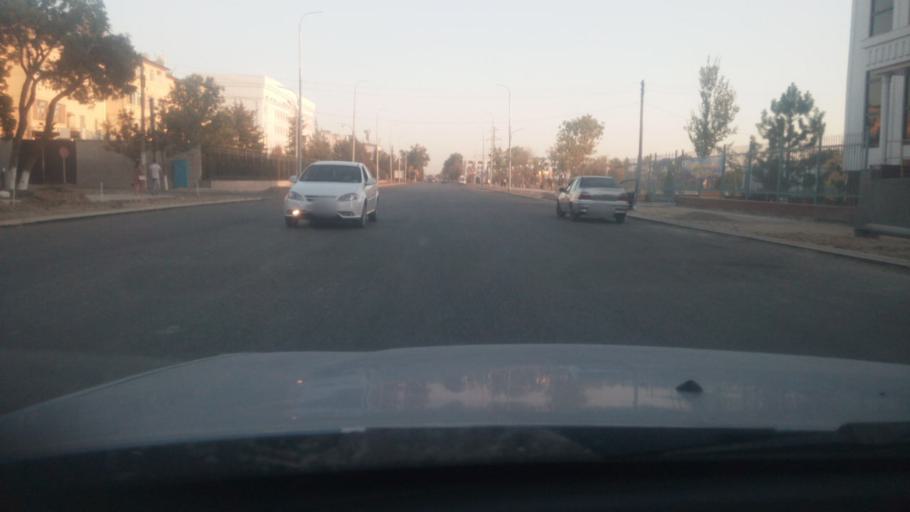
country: UZ
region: Sirdaryo
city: Guliston
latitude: 40.5016
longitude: 68.7755
